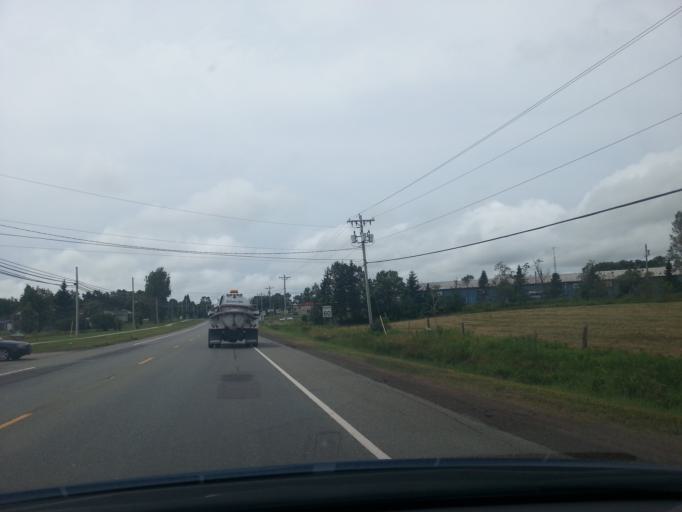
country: CA
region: Prince Edward Island
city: Charlottetown
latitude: 46.2873
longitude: -63.0915
